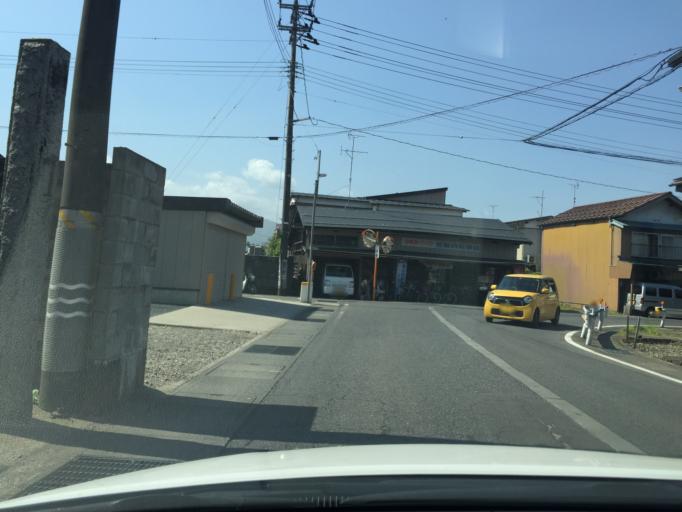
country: JP
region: Niigata
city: Muramatsu
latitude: 37.6895
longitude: 139.1756
